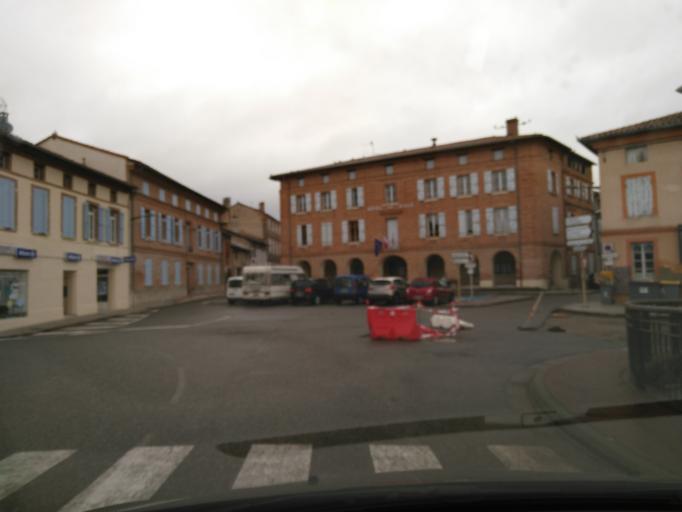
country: FR
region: Midi-Pyrenees
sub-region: Departement de la Haute-Garonne
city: Montesquieu-Volvestre
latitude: 43.2062
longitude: 1.2284
